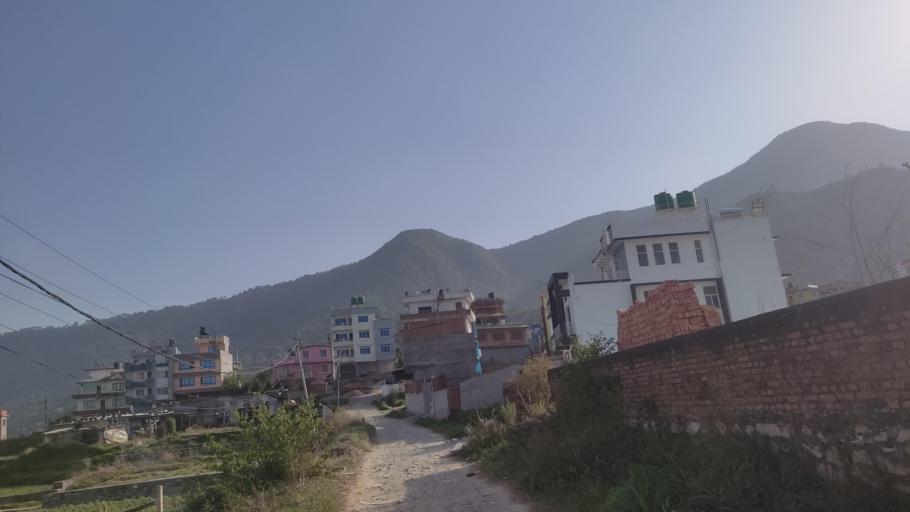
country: NP
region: Central Region
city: Kirtipur
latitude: 27.6565
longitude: 85.2779
